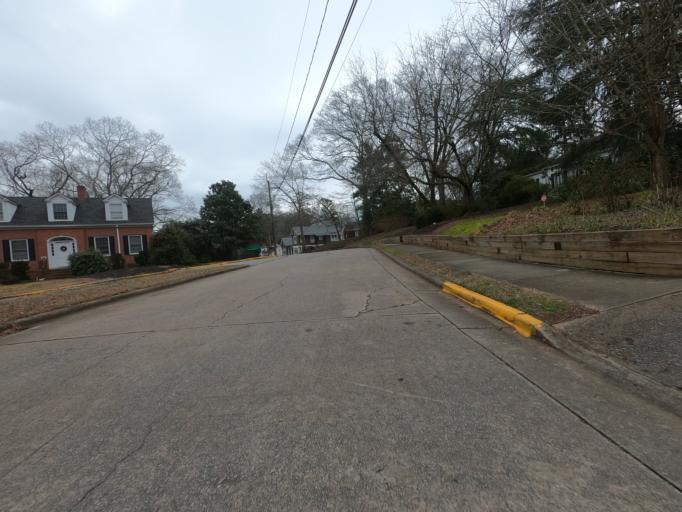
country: US
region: Georgia
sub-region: Clarke County
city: Athens
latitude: 33.9387
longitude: -83.3844
